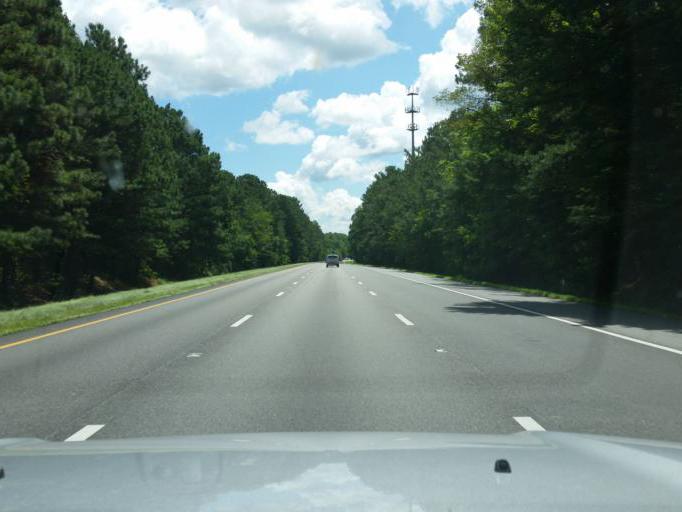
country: US
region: Virginia
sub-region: King William County
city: West Point
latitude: 37.4207
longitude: -76.8232
